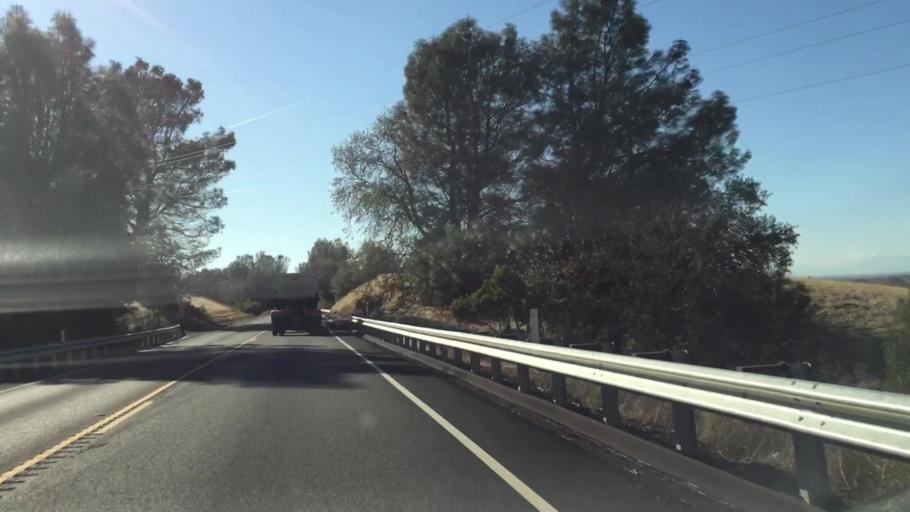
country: US
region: California
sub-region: Butte County
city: Thermalito
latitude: 39.6339
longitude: -121.5835
